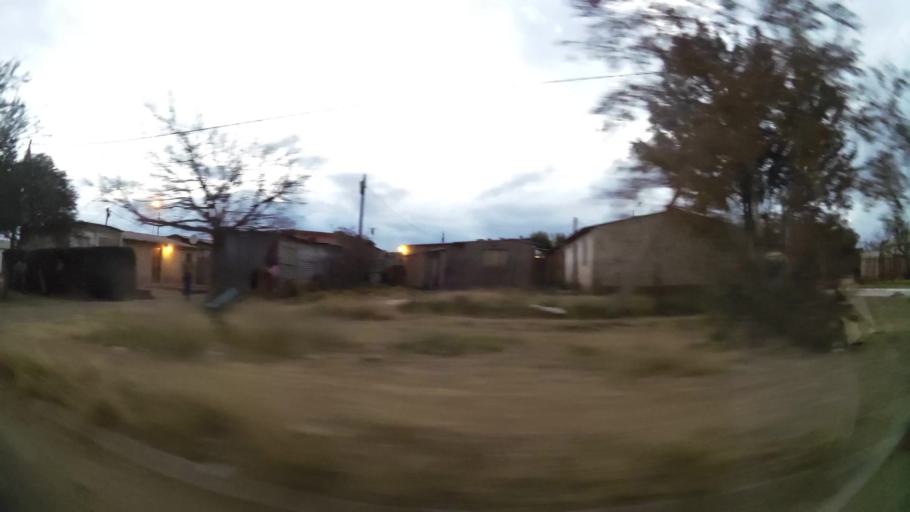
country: ZA
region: Orange Free State
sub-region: Lejweleputswa District Municipality
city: Welkom
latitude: -27.9570
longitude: 26.7855
